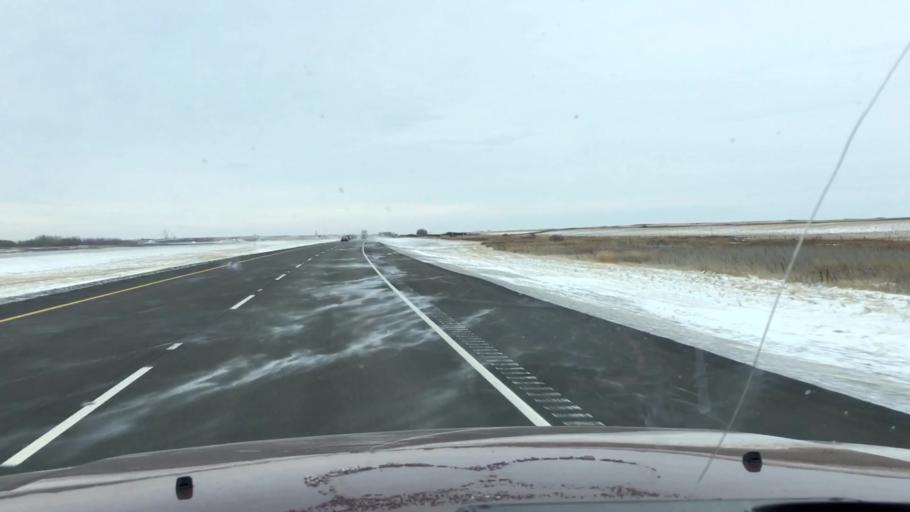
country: CA
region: Saskatchewan
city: Moose Jaw
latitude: 50.8966
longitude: -105.6304
